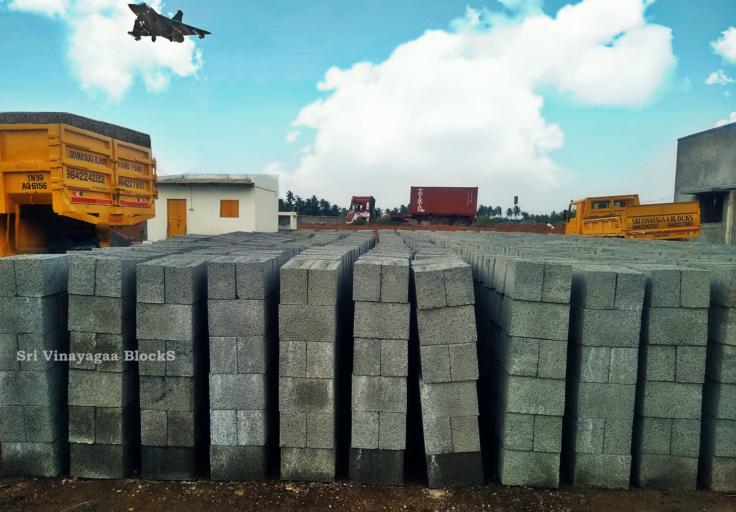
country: IN
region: Tamil Nadu
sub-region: Coimbatore
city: Sulur
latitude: 11.0250
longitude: 77.1721
